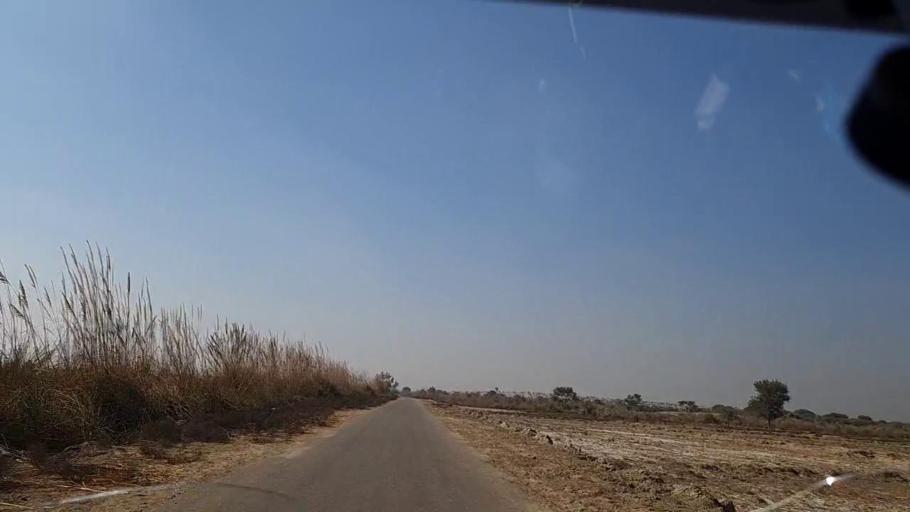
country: PK
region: Sindh
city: Khanpur
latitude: 27.5664
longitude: 69.3869
